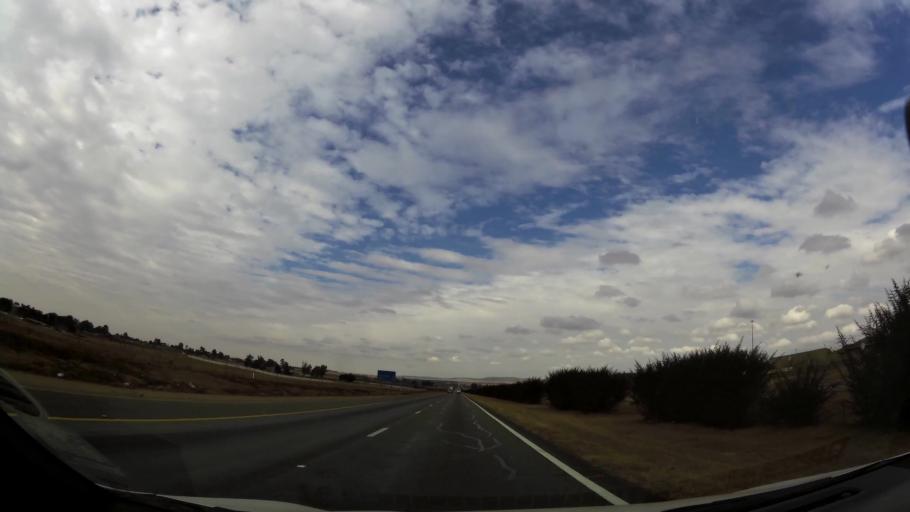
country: ZA
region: Gauteng
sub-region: Ekurhuleni Metropolitan Municipality
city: Germiston
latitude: -26.3550
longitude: 28.2310
